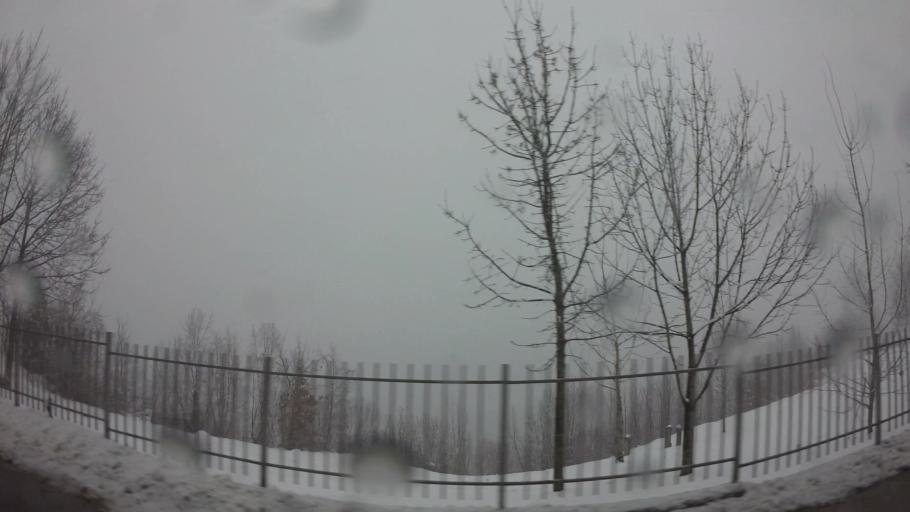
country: BA
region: Federation of Bosnia and Herzegovina
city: Kobilja Glava
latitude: 43.8542
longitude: 18.4457
